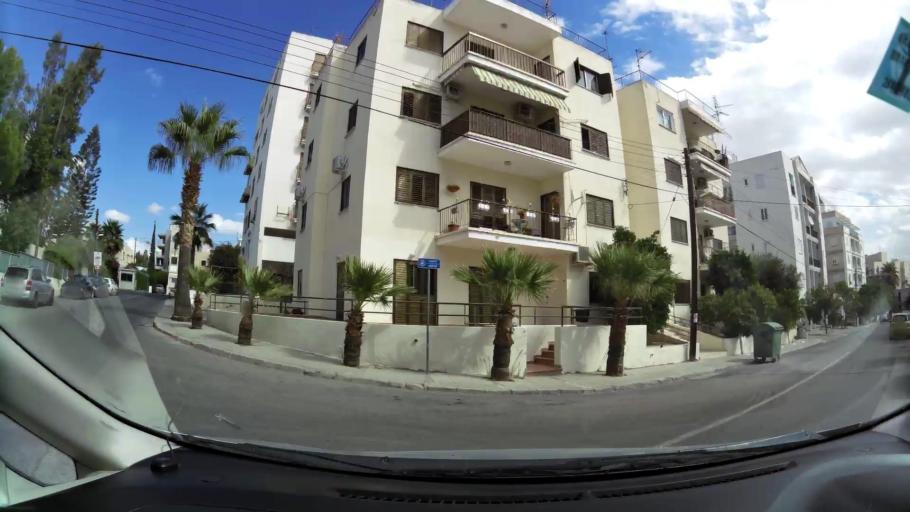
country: CY
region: Lefkosia
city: Nicosia
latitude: 35.1522
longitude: 33.3678
